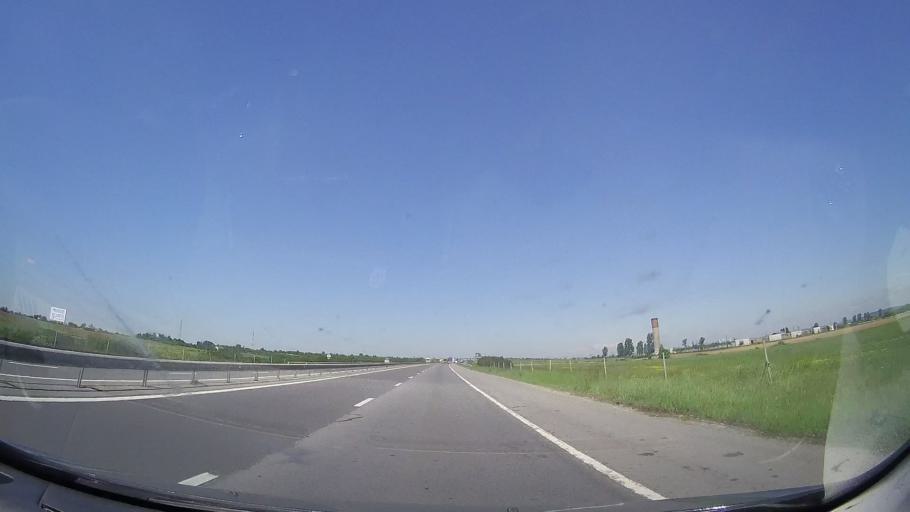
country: RO
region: Arges
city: Popesti
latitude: 44.7615
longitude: 25.0508
